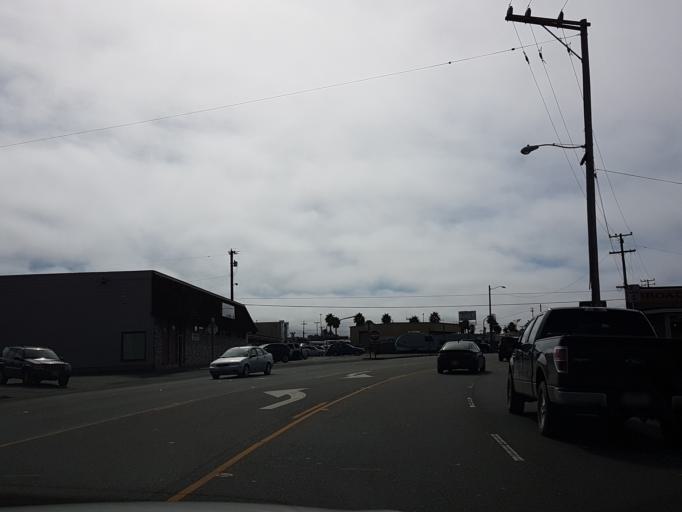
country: US
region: California
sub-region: Humboldt County
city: Eureka
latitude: 40.7974
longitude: -124.1752
